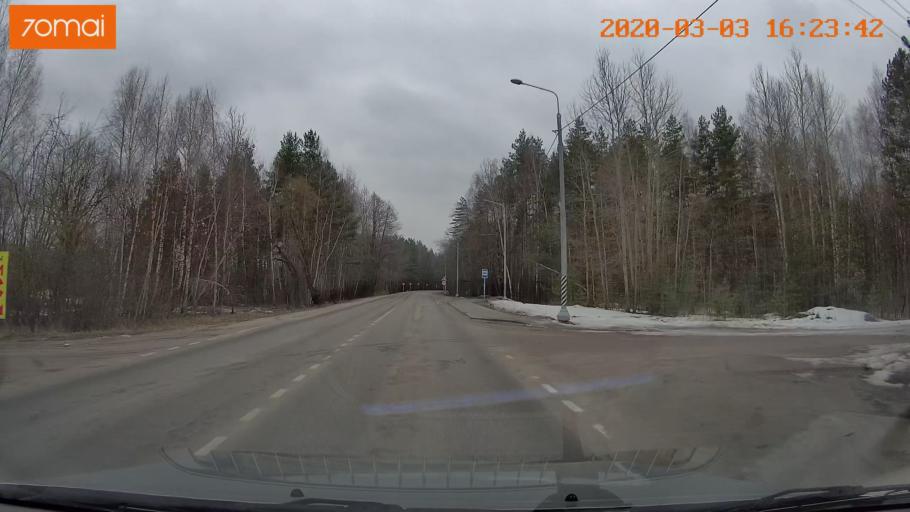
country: RU
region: Moskovskaya
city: Imeni Tsyurupy
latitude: 55.4772
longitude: 38.6561
